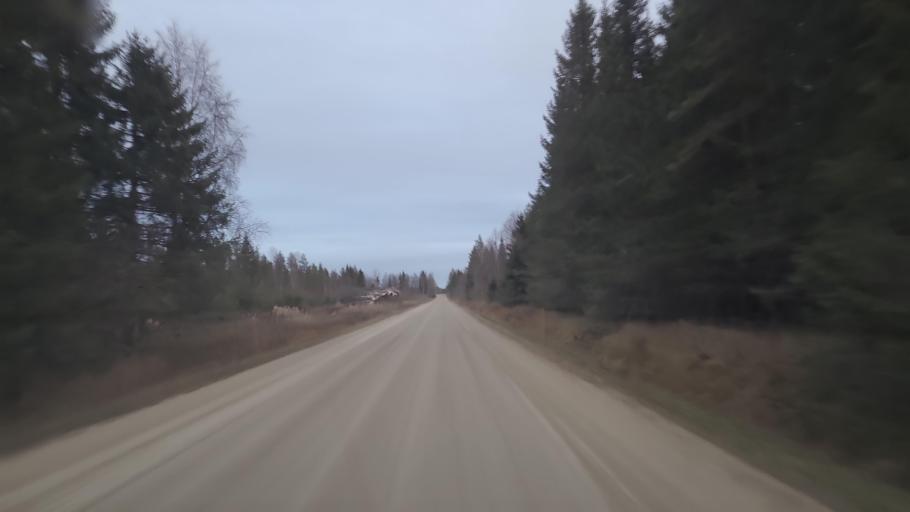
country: FI
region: Lapland
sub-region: Kemi-Tornio
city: Tervola
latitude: 66.0732
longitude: 24.8549
